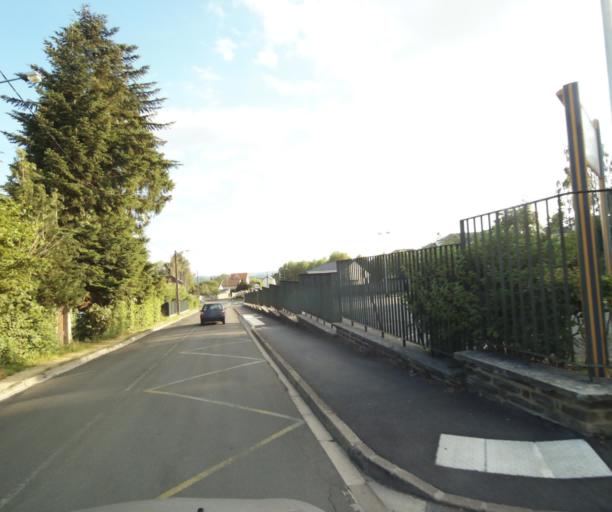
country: FR
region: Champagne-Ardenne
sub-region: Departement des Ardennes
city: Charleville-Mezieres
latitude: 49.7873
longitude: 4.7223
